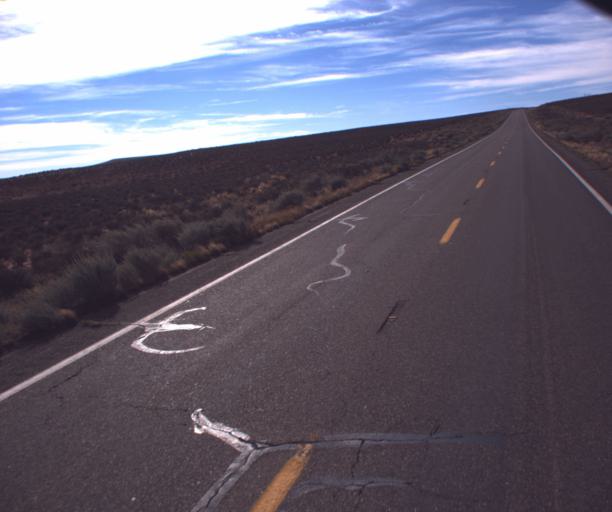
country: US
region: Arizona
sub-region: Coconino County
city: LeChee
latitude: 36.8194
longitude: -111.3075
